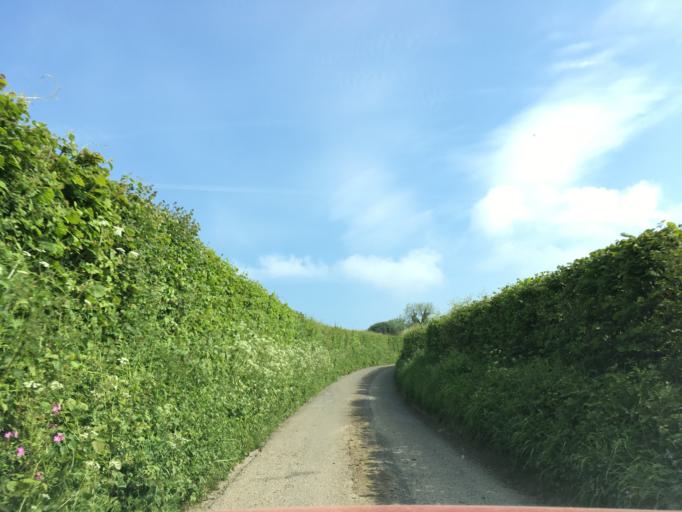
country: GB
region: England
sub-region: North Somerset
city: Dundry
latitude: 51.3899
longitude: -2.6494
